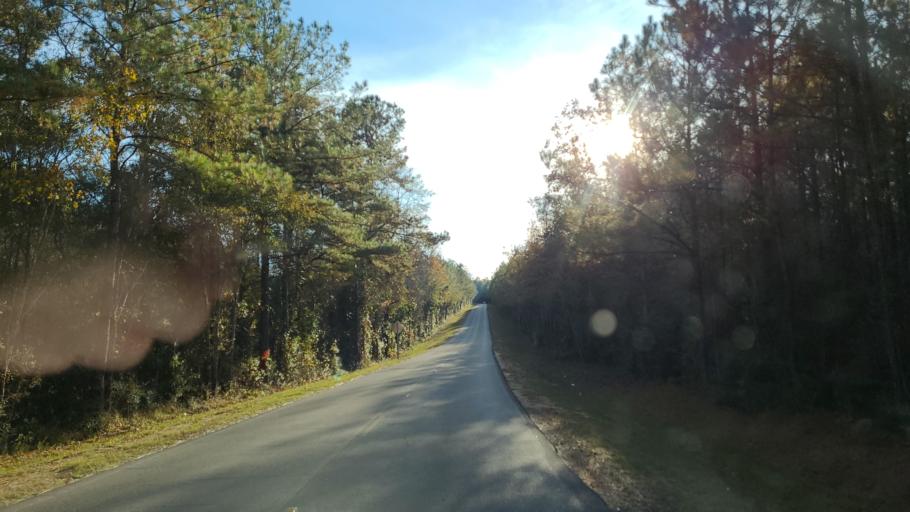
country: US
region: Mississippi
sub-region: Lamar County
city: Purvis
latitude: 31.1516
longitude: -89.3357
